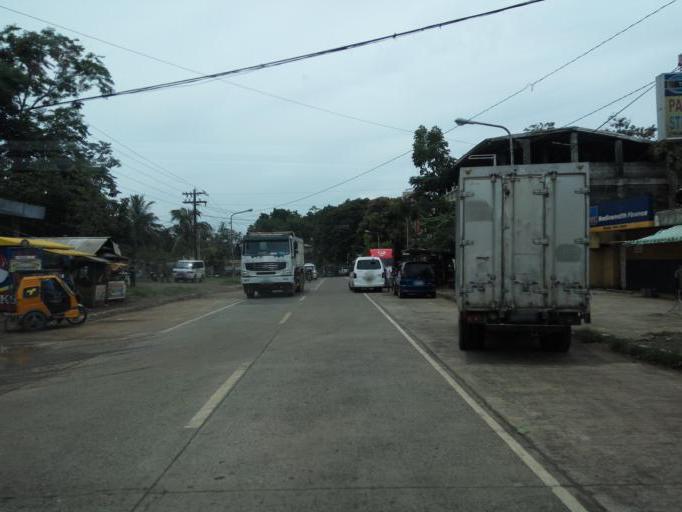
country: PH
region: Cagayan Valley
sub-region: Province of Quirino
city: Diffun
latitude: 16.5924
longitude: 121.5026
